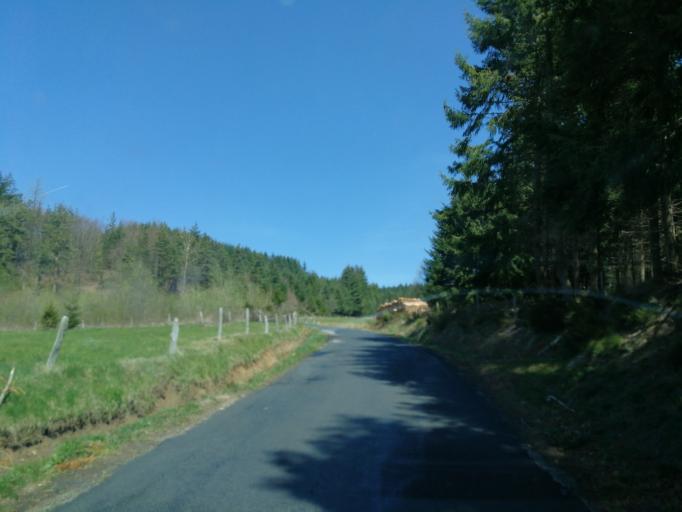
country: FR
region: Rhone-Alpes
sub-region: Departement de l'Ardeche
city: Le Cheylard
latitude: 44.9506
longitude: 4.4182
